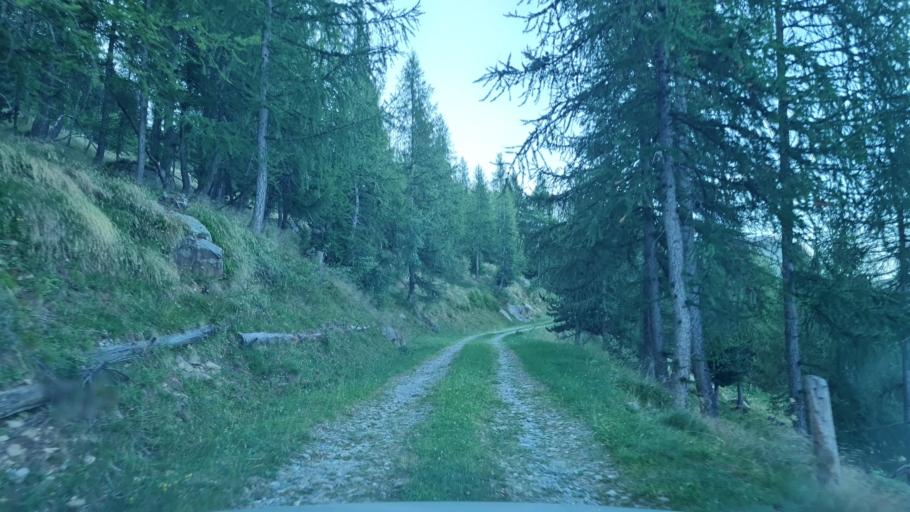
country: IT
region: Aosta Valley
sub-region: Valle d'Aosta
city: Fontainemore
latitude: 45.6203
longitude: 7.8776
